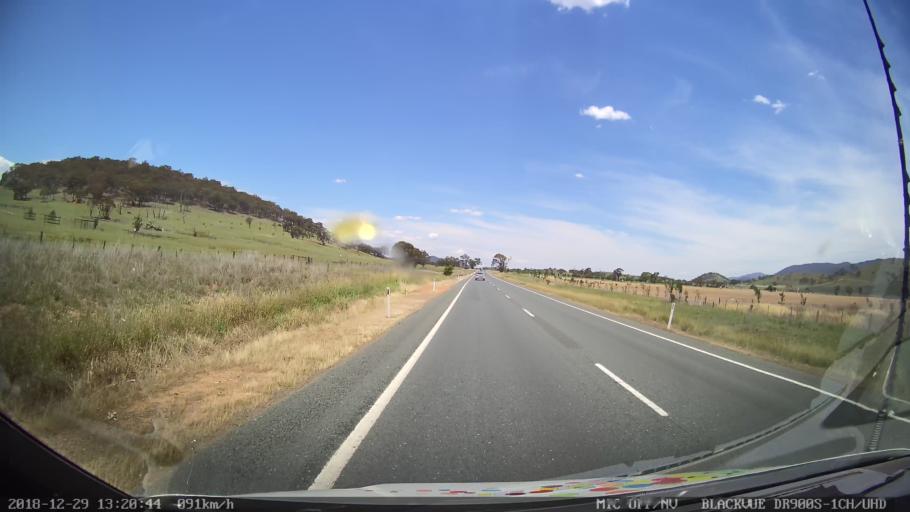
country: AU
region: Australian Capital Territory
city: Macarthur
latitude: -35.7829
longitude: 149.1621
